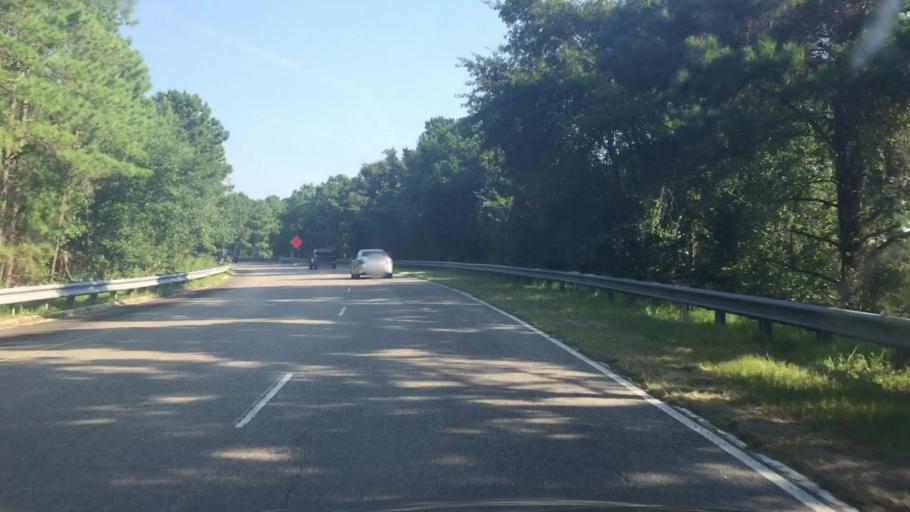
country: US
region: South Carolina
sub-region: Horry County
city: Little River
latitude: 33.8619
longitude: -78.6569
